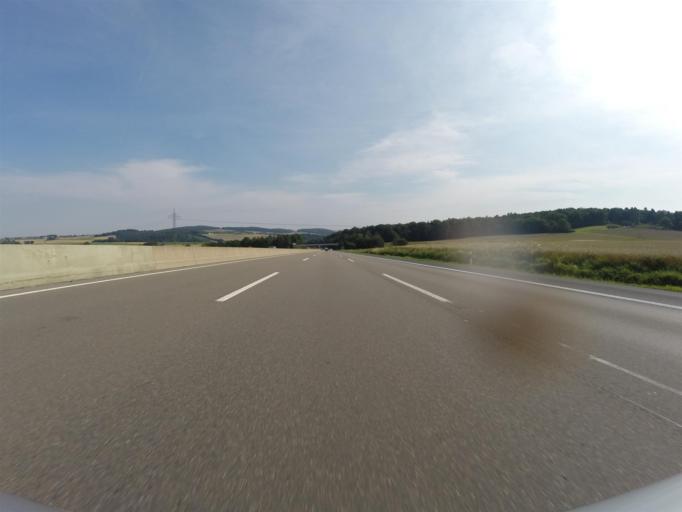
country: DE
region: Hesse
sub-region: Regierungsbezirk Kassel
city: Malsfeld
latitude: 51.0570
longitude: 9.4957
